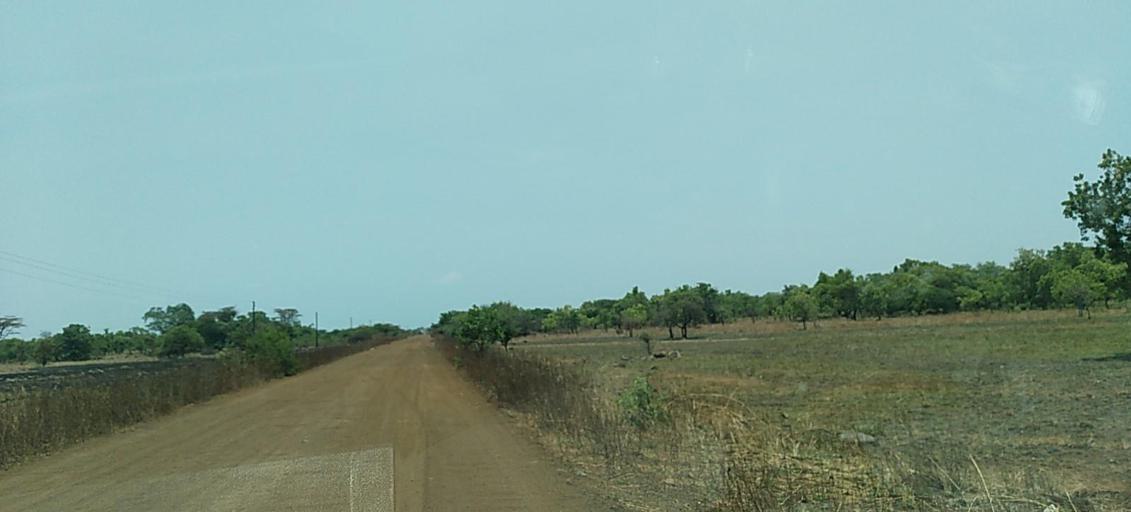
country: ZM
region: Copperbelt
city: Mpongwe
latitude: -13.7173
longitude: 27.8685
